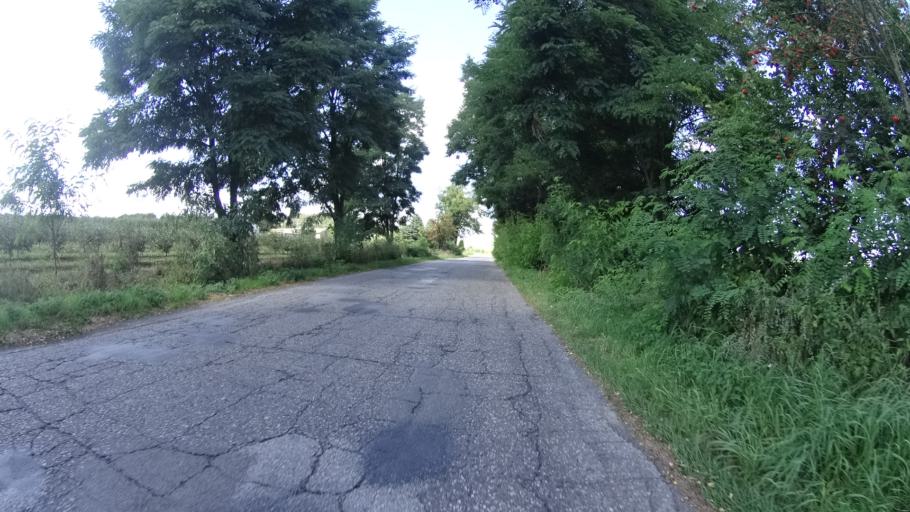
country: PL
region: Masovian Voivodeship
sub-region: Powiat grojecki
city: Mogielnica
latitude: 51.6670
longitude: 20.7402
